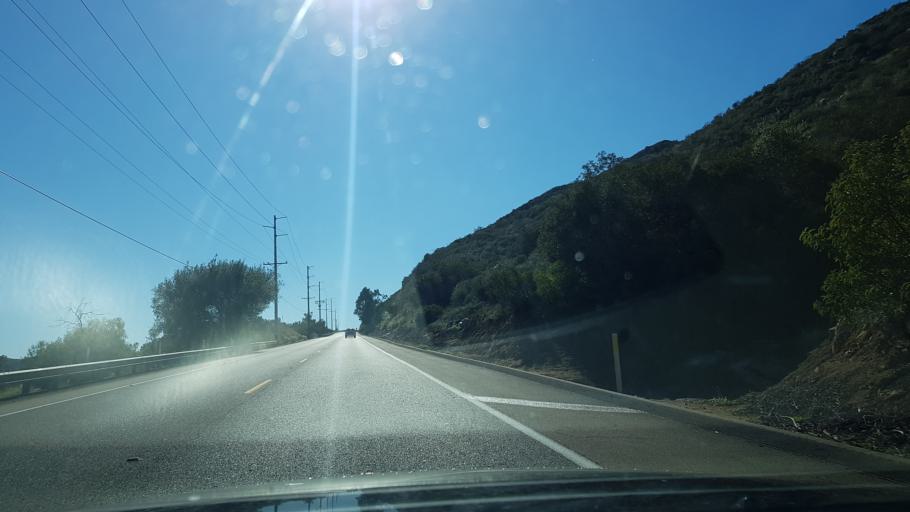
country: US
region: California
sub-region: San Diego County
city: Escondido
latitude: 33.0774
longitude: -117.1208
